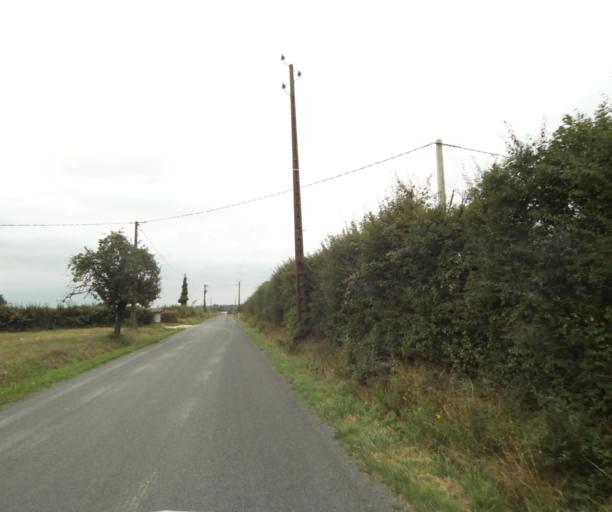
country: FR
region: Pays de la Loire
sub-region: Departement de la Sarthe
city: Sable-sur-Sarthe
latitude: 47.8181
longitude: -0.3380
